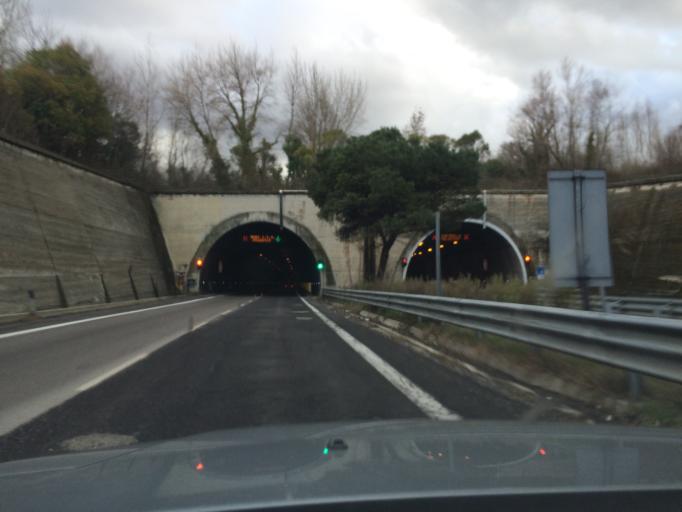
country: IT
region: Umbria
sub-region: Provincia di Terni
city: San Gemini
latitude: 42.6351
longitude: 12.5460
